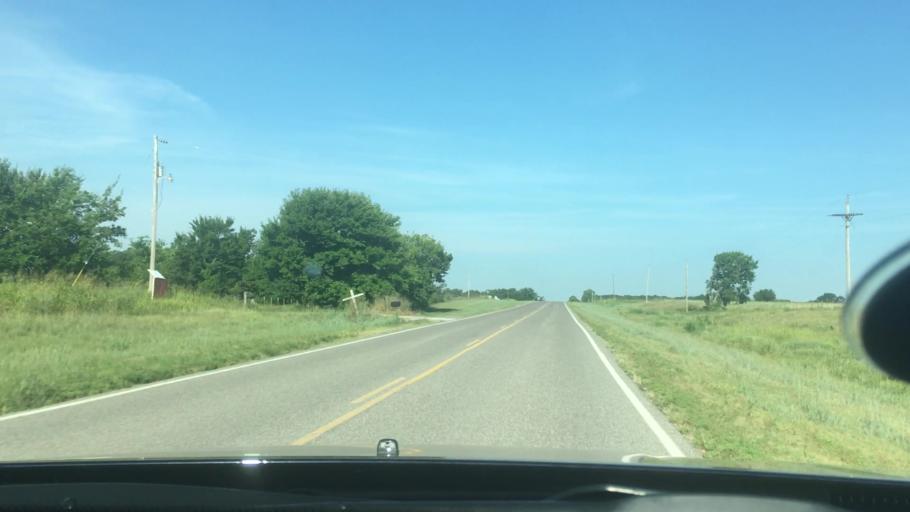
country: US
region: Oklahoma
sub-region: Garvin County
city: Pauls Valley
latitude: 34.6521
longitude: -97.3323
